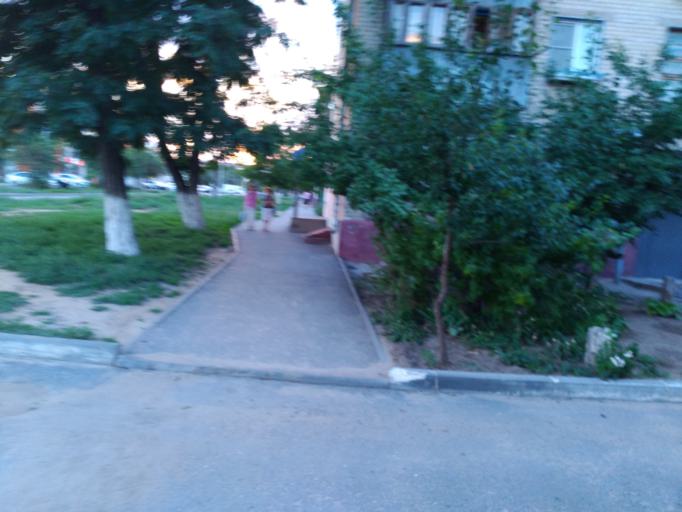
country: RU
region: Volgograd
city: Volgograd
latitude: 48.6731
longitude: 44.4466
